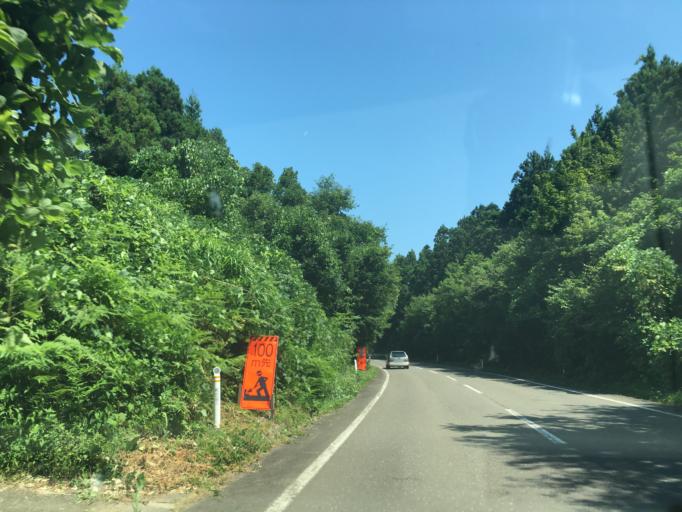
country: JP
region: Akita
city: Tenno
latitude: 39.9784
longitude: 139.7288
